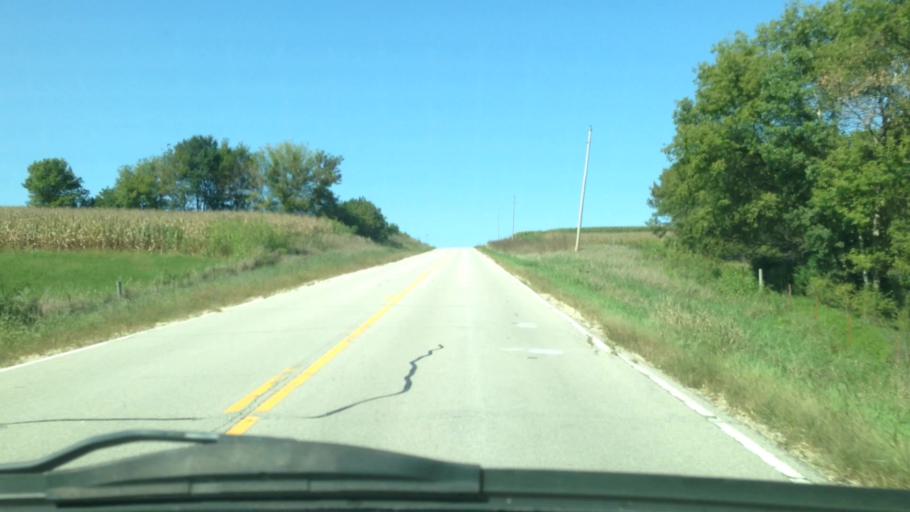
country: US
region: Minnesota
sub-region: Fillmore County
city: Rushford
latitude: 43.6968
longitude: -91.7702
